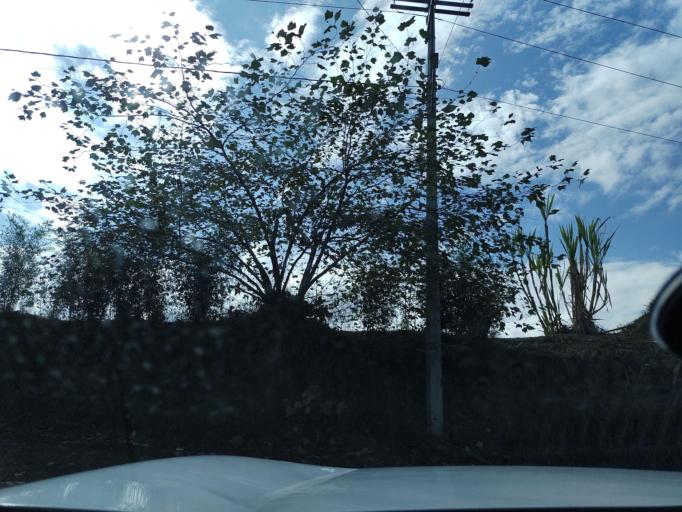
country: MX
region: Veracruz
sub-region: Coatepec
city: Las Lomas
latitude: 19.4810
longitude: -96.9307
